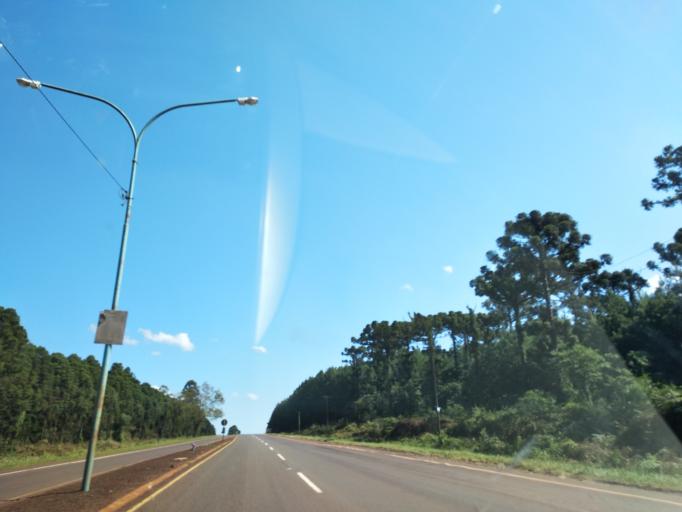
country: AR
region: Misiones
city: Puerto Piray
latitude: -26.4932
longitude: -54.6753
